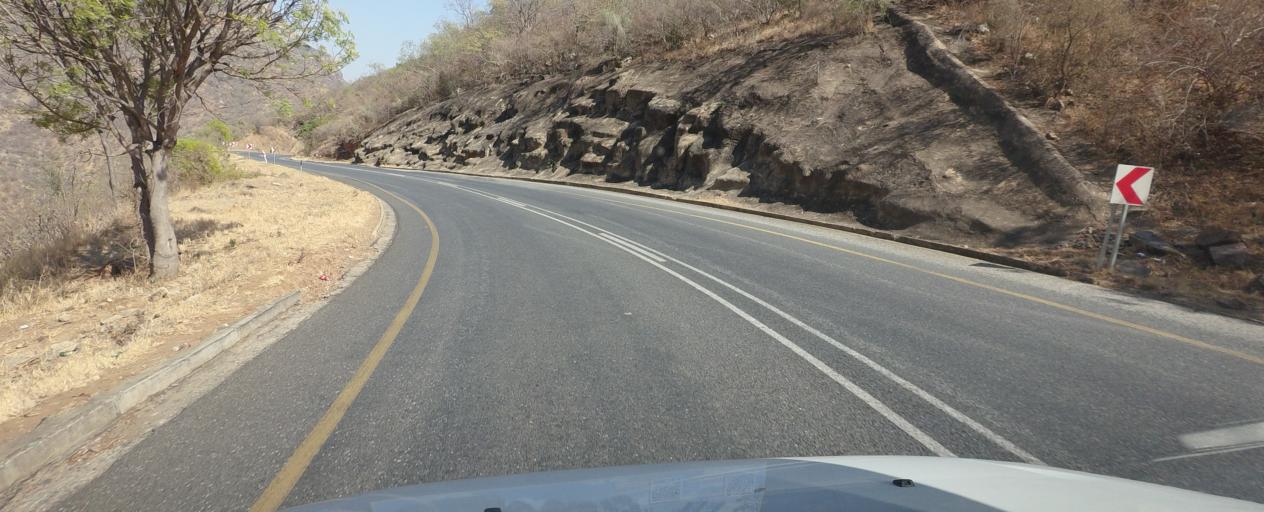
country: ZA
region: Limpopo
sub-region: Mopani District Municipality
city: Hoedspruit
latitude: -24.4524
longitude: 30.6130
